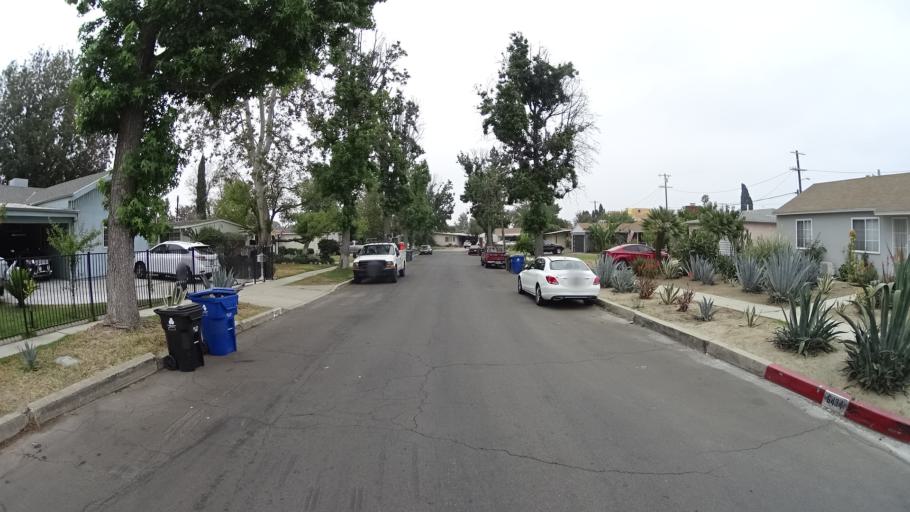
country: US
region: California
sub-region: Los Angeles County
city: Van Nuys
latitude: 34.1875
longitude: -118.4202
